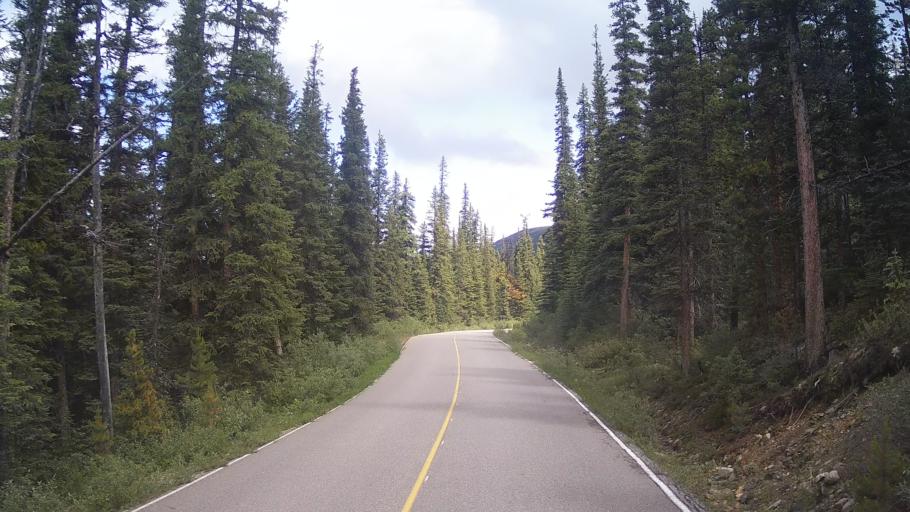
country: CA
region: Alberta
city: Jasper Park Lodge
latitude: 52.7159
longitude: -118.0549
